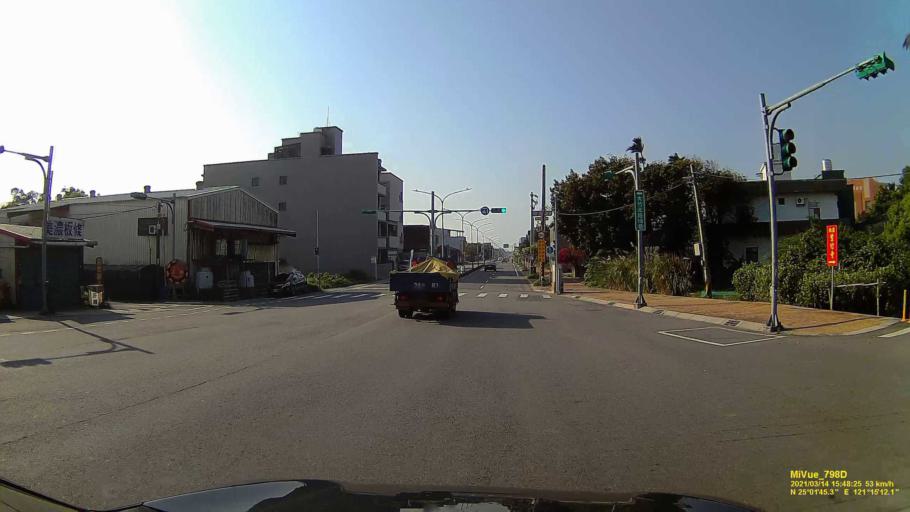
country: TW
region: Taiwan
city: Taoyuan City
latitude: 25.0294
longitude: 121.2531
